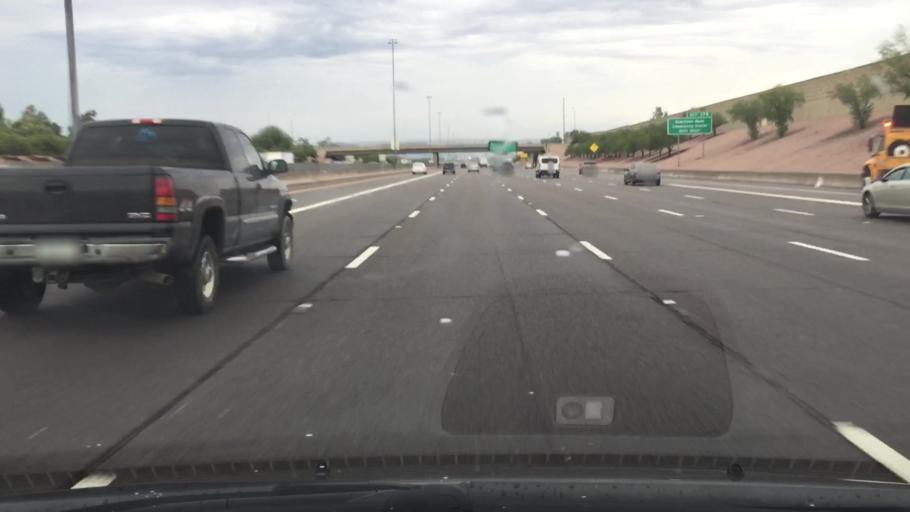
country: US
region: Arizona
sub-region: Maricopa County
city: San Carlos
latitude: 33.3864
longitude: -111.8515
